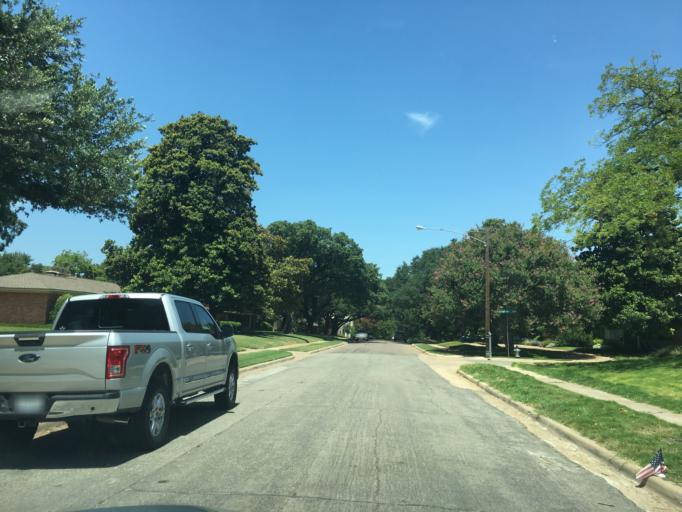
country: US
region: Texas
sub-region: Dallas County
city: Highland Park
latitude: 32.8460
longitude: -96.7356
